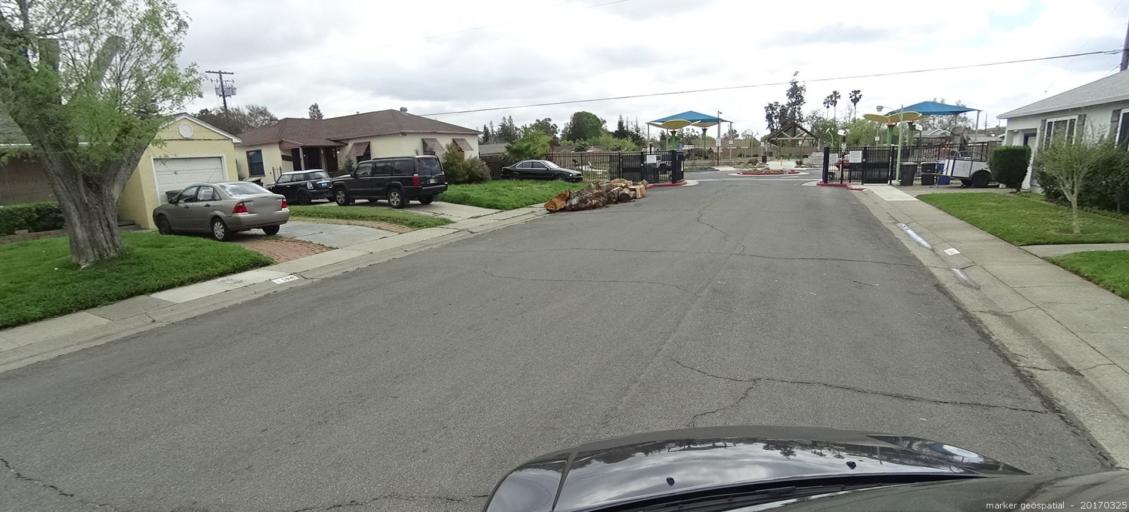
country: US
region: California
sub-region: Sacramento County
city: Florin
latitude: 38.5181
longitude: -121.4338
